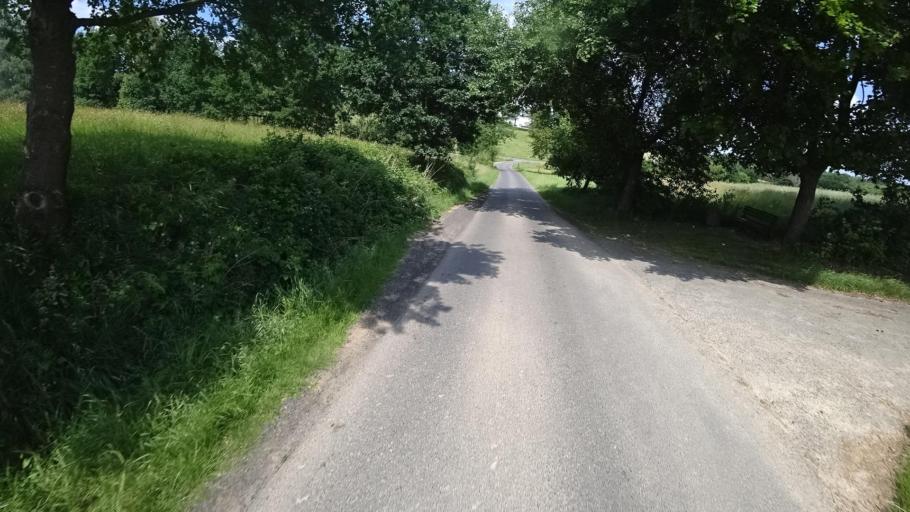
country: DE
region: Rheinland-Pfalz
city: Helmenzen
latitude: 50.7055
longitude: 7.6267
